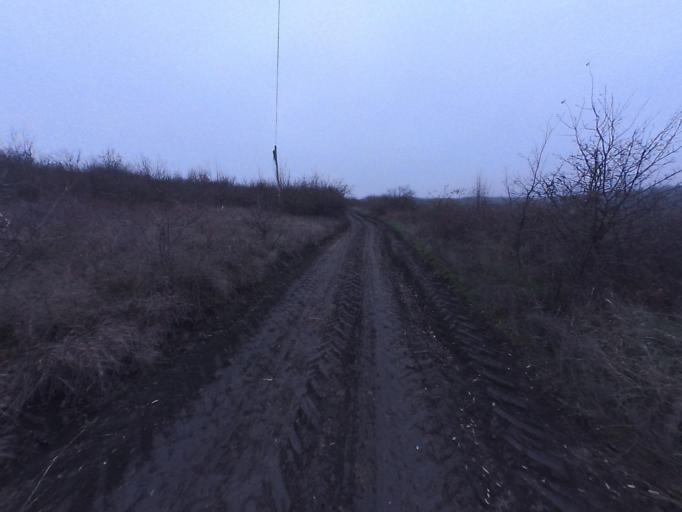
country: RO
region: Galati
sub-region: Comuna Balabanesti
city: Balabanesti
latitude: 46.1451
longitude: 27.7407
